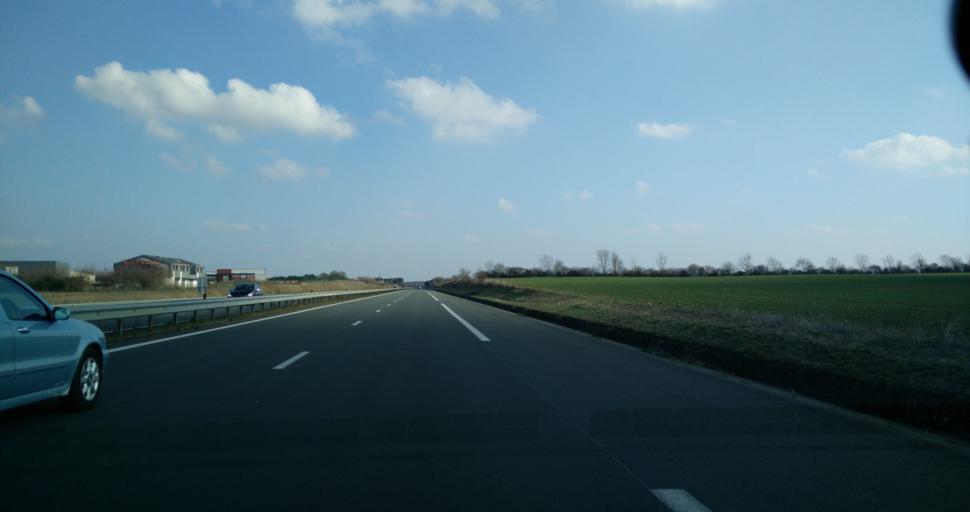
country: FR
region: Poitou-Charentes
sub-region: Departement de la Charente-Maritime
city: Saint-Jean-de-Liversay
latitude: 46.2263
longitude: -0.8731
